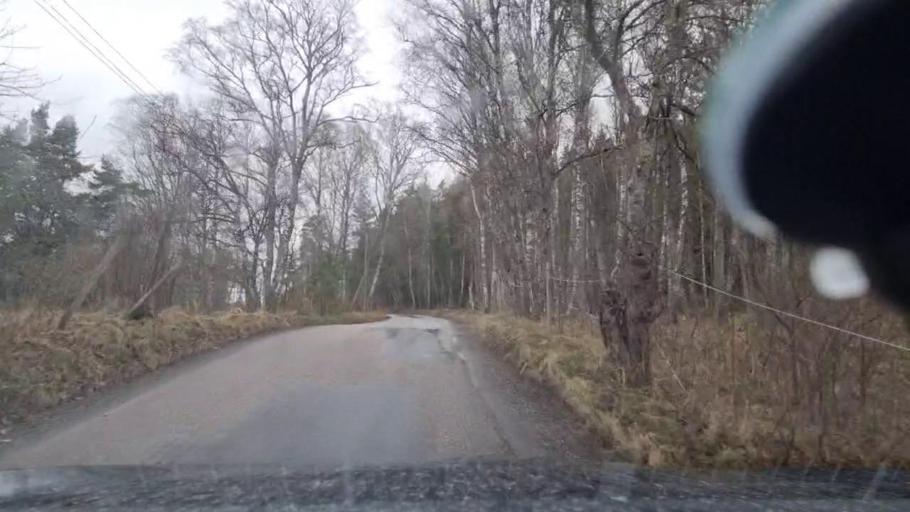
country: SE
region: Stockholm
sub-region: Taby Kommun
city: Taby
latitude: 59.4852
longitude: 18.0134
